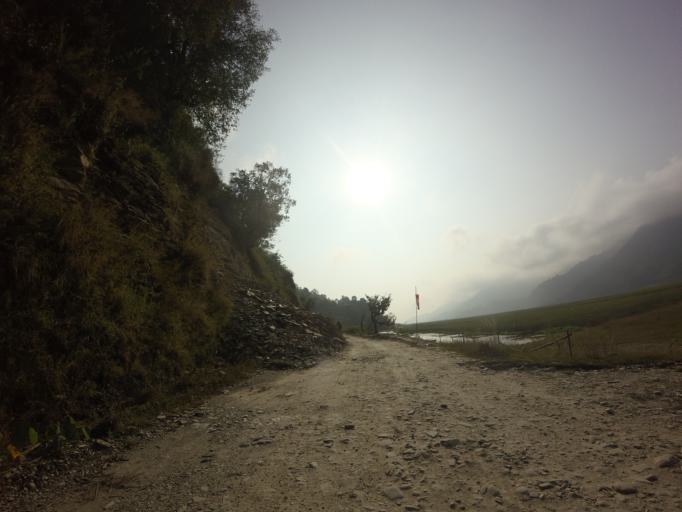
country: NP
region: Western Region
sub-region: Gandaki Zone
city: Pokhara
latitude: 28.2345
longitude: 83.9150
